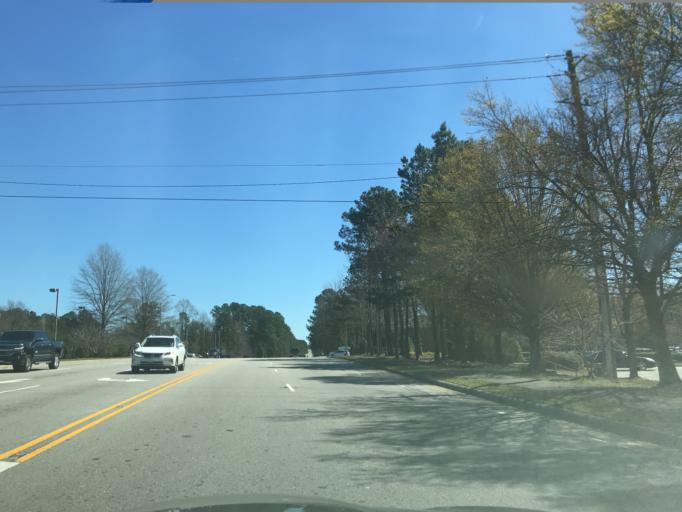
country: US
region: North Carolina
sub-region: Wake County
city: Garner
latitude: 35.6861
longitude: -78.6173
